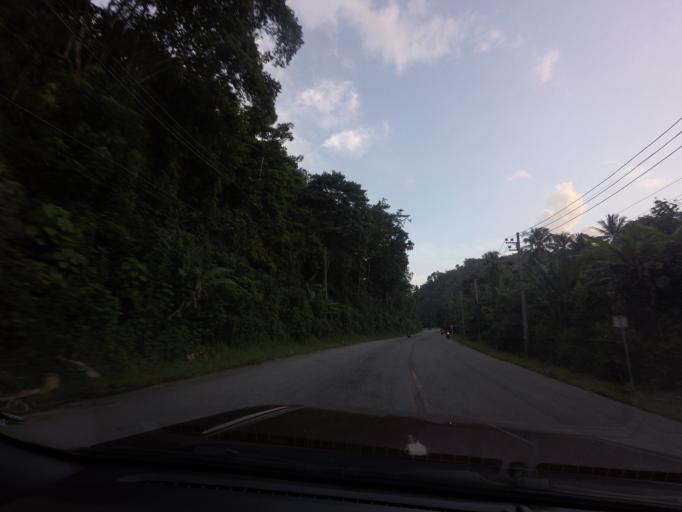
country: TH
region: Yala
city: Than To
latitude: 6.0668
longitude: 101.1978
